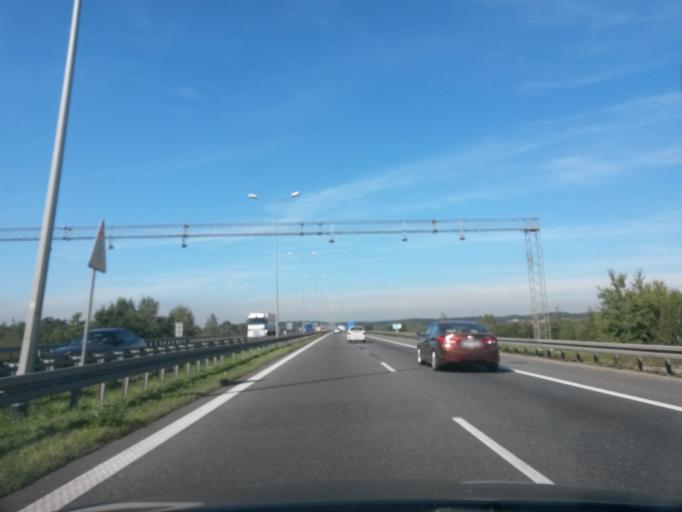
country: PL
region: Lesser Poland Voivodeship
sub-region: Powiat krakowski
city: Piekary
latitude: 50.0237
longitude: 19.8256
